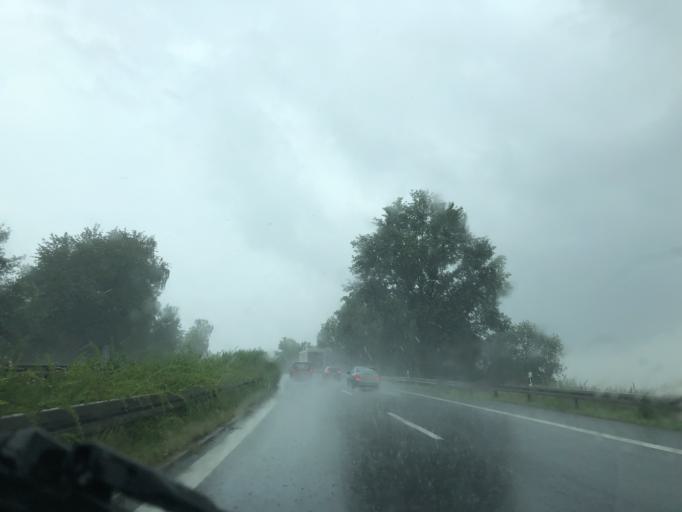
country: DE
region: Bavaria
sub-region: Upper Bavaria
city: Wolnzach
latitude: 48.5838
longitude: 11.5989
